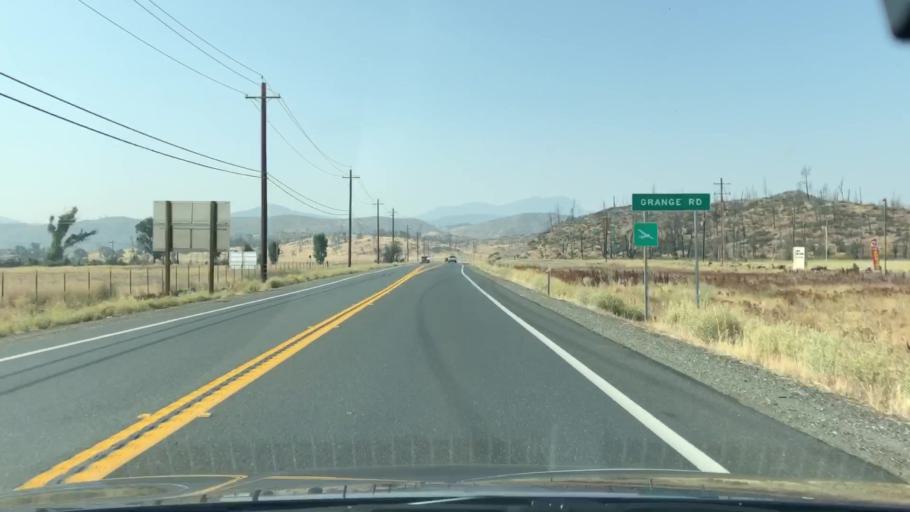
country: US
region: California
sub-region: Lake County
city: Hidden Valley Lake
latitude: 38.7859
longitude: -122.5681
